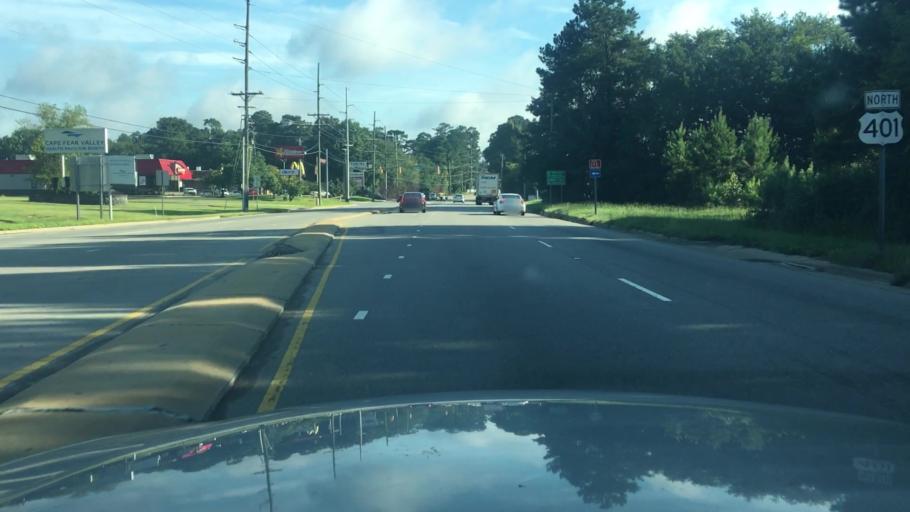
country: US
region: North Carolina
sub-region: Cumberland County
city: Eastover
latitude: 35.1559
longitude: -78.8695
